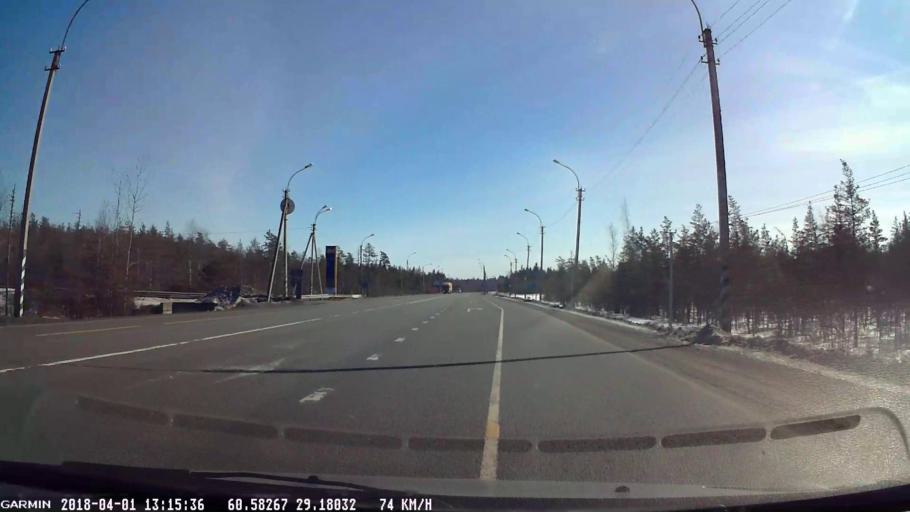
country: RU
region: Leningrad
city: Veshchevo
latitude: 60.5826
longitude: 29.1805
